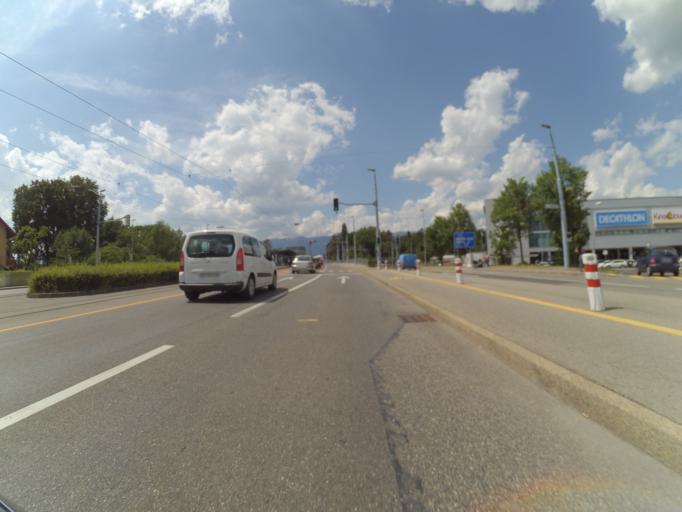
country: CH
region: Geneva
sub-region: Geneva
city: Vernier
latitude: 46.2256
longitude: 6.0844
